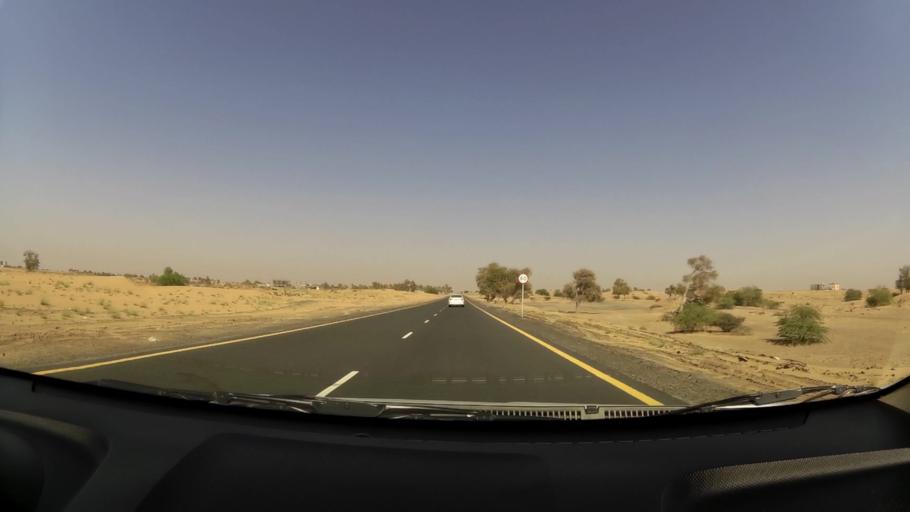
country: AE
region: Umm al Qaywayn
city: Umm al Qaywayn
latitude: 25.4801
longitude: 55.6172
